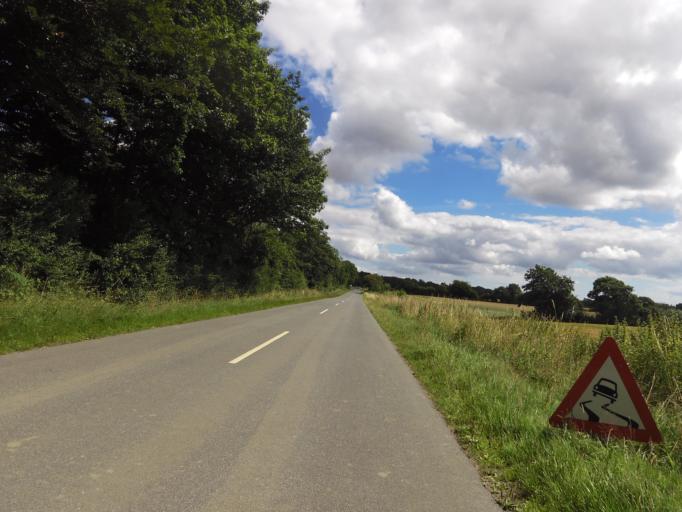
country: DK
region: South Denmark
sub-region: Haderslev Kommune
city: Vojens
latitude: 55.2840
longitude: 9.3903
